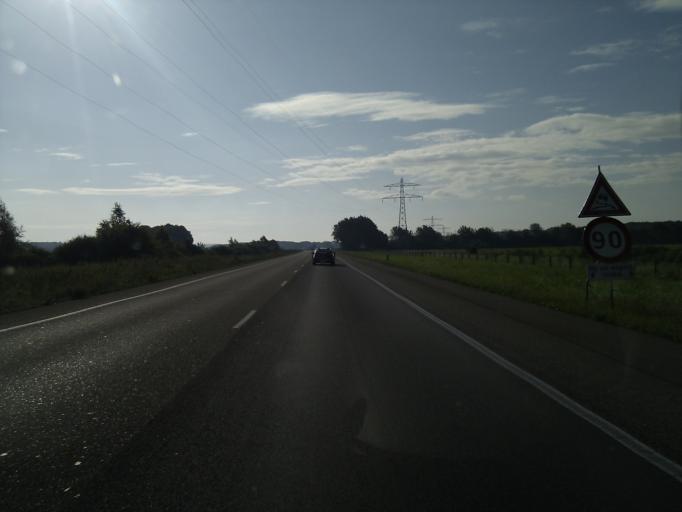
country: NL
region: Gelderland
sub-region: Gemeente Nijmegen
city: Lindenholt
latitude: 51.7885
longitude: 5.8155
